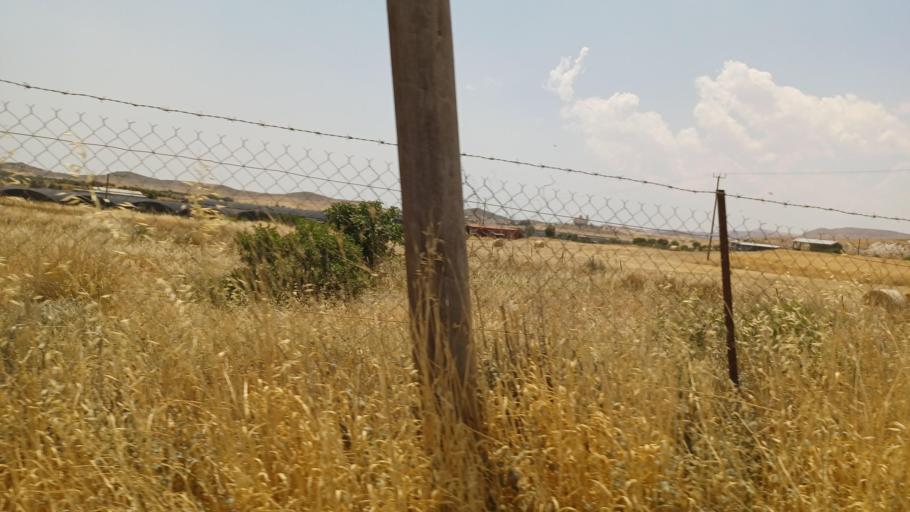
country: CY
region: Larnaka
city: Troulloi
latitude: 35.0338
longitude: 33.6032
